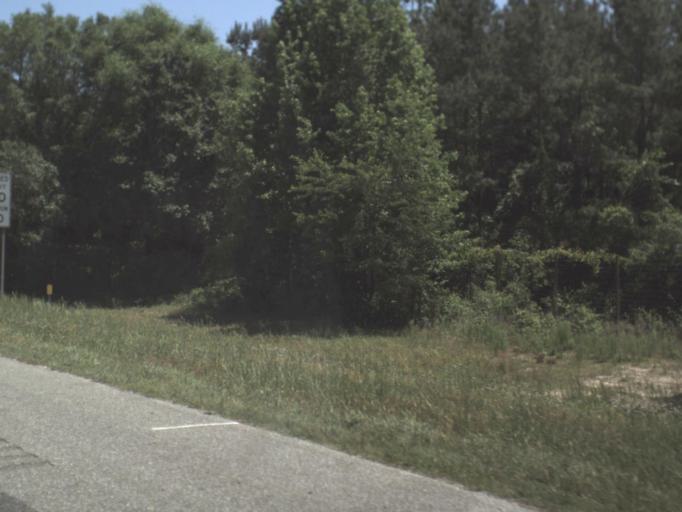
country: US
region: Florida
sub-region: Jefferson County
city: Monticello
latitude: 30.4734
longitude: -83.8780
